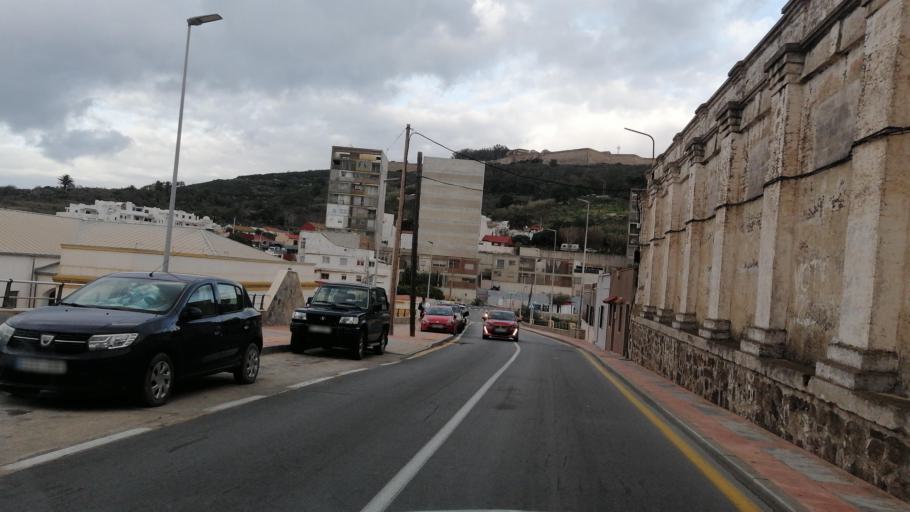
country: ES
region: Ceuta
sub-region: Ceuta
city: Ceuta
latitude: 35.8904
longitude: -5.2983
